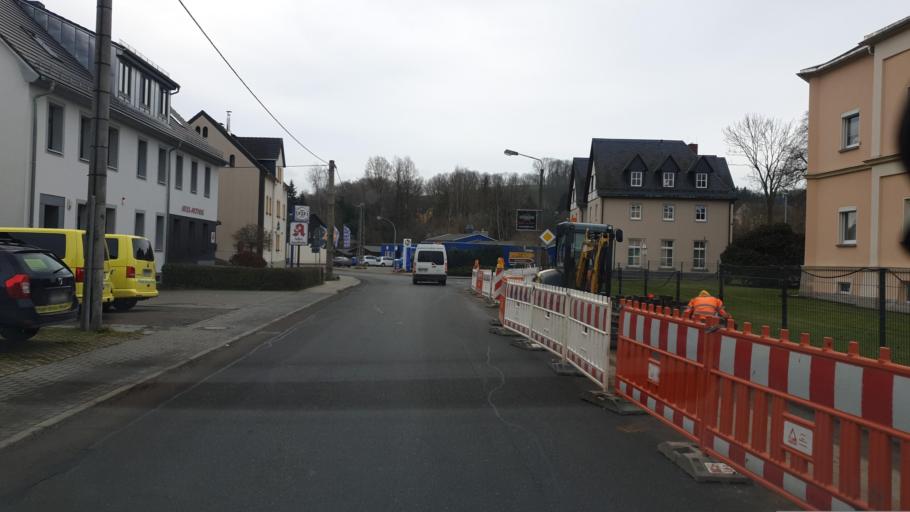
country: DE
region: Saxony
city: Mulda
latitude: 50.8090
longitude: 13.4081
